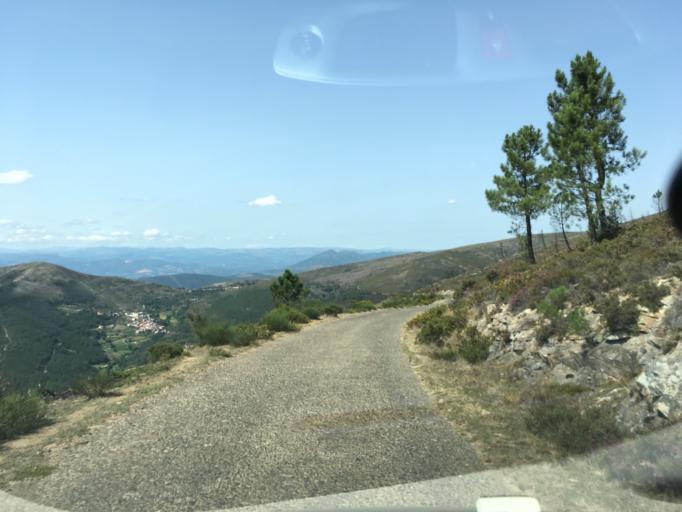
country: PT
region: Braga
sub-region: Celorico de Basto
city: Celorico de Basto
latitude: 41.2781
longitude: -7.9477
